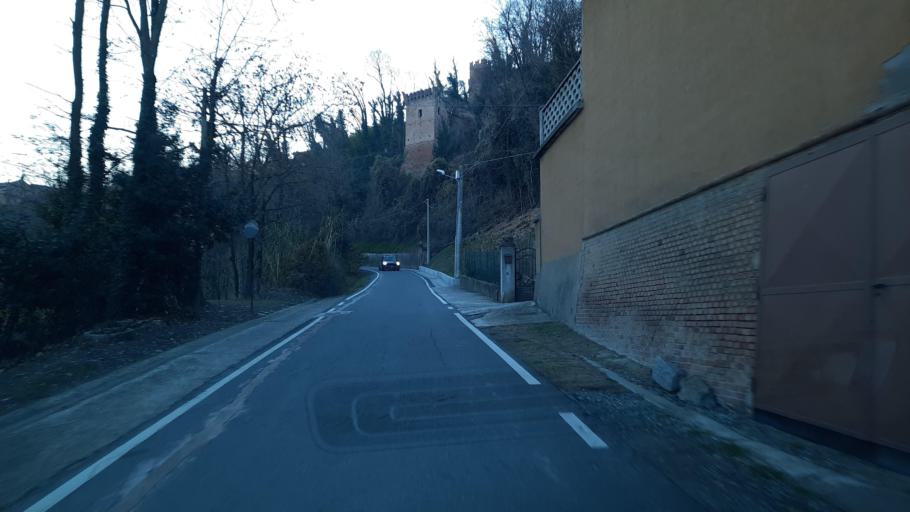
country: IT
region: Piedmont
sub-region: Provincia di Alessandria
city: Camino
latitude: 45.1626
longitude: 8.2832
